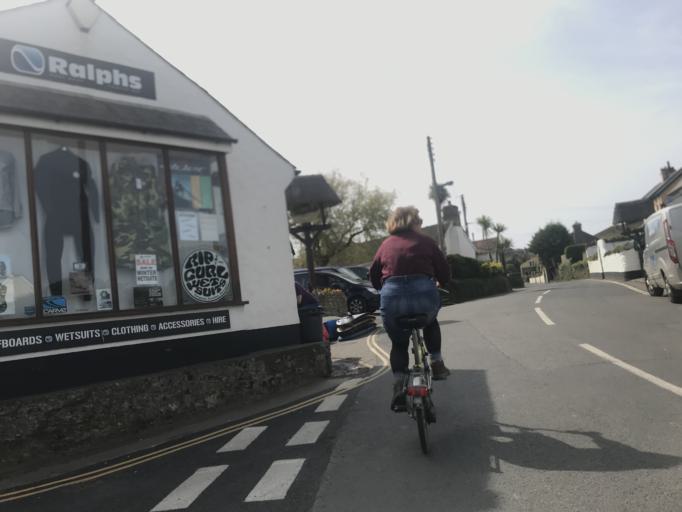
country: GB
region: England
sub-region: Devon
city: Braunton
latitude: 51.1299
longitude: -4.2246
